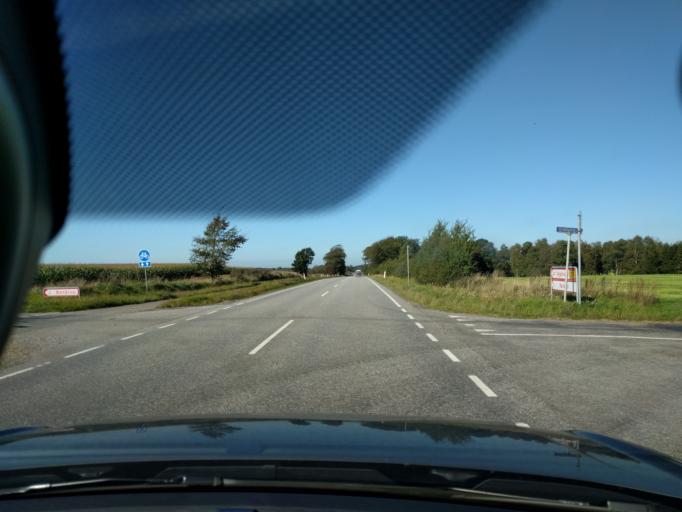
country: DK
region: North Denmark
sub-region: Mariagerfjord Kommune
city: Hobro
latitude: 56.6869
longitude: 9.6562
